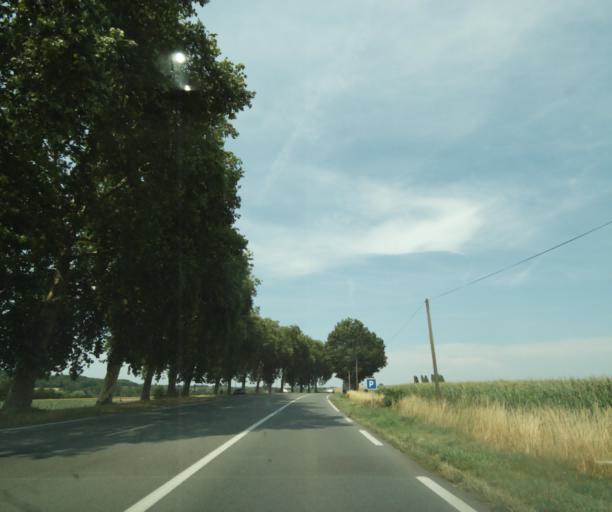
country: FR
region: Poitou-Charentes
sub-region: Departement de la Vienne
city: Antran
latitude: 46.8942
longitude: 0.5696
